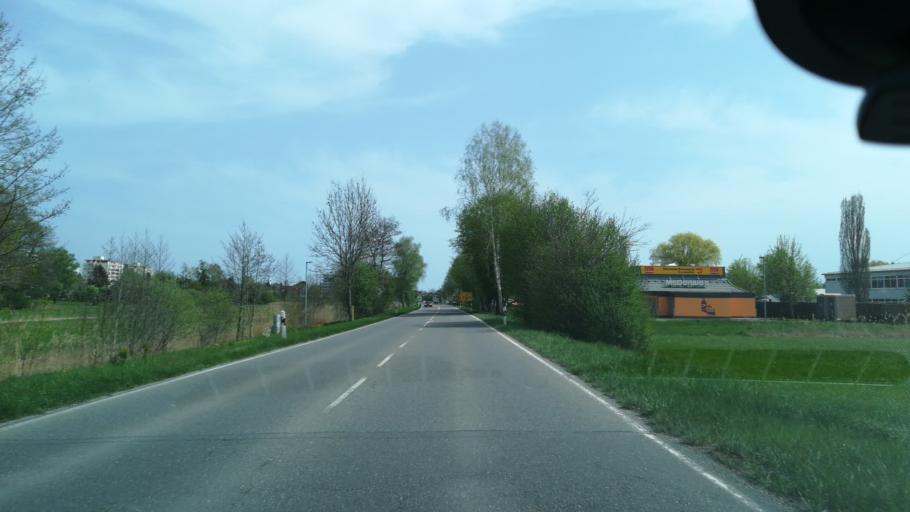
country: DE
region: Baden-Wuerttemberg
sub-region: Freiburg Region
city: Moos
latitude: 47.7486
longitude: 8.9494
